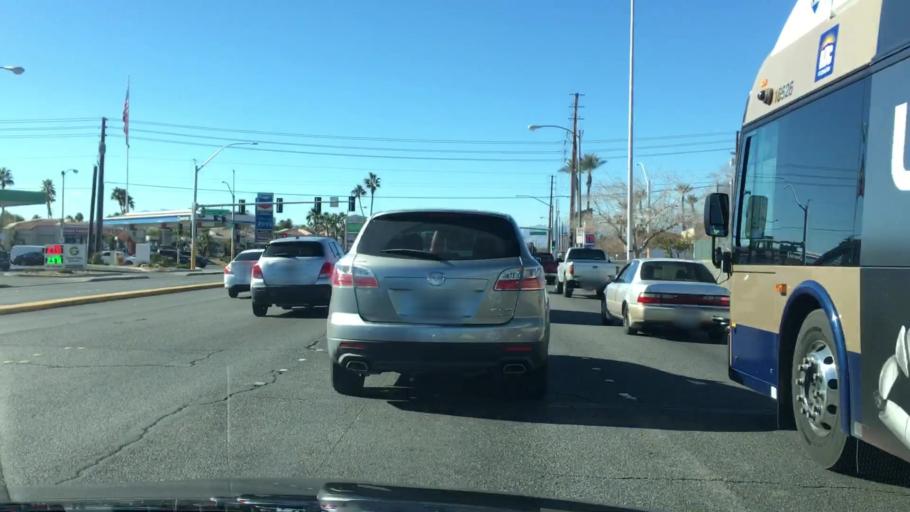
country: US
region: Nevada
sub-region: Clark County
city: Whitney
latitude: 36.0570
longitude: -115.1173
